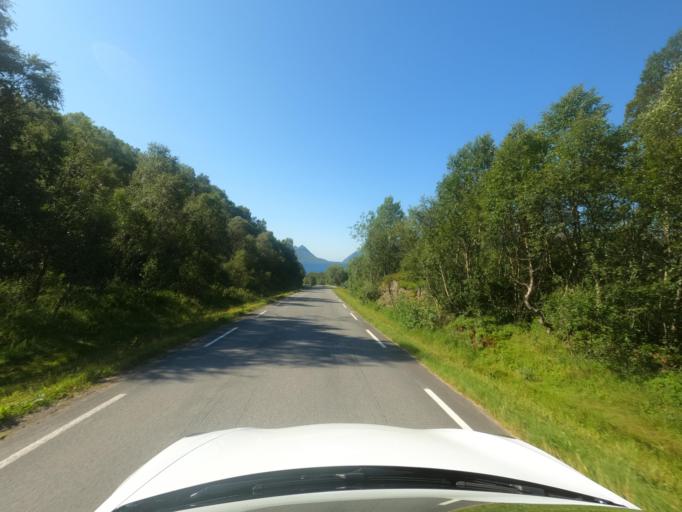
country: NO
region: Nordland
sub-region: Hadsel
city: Stokmarknes
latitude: 68.3496
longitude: 15.0617
